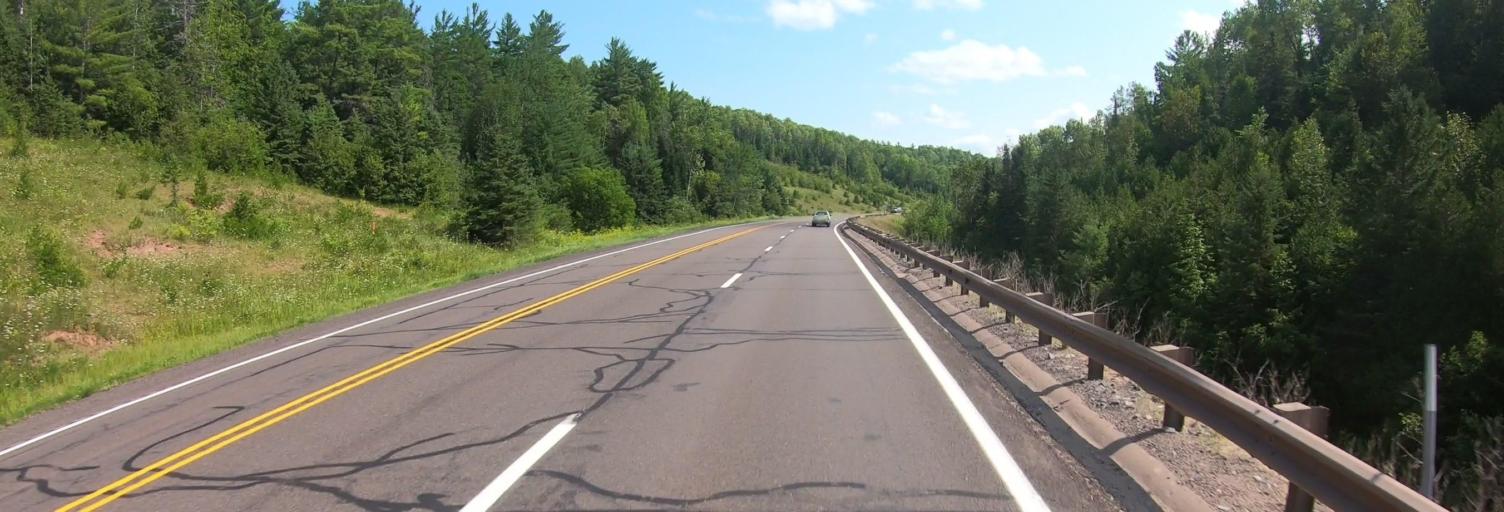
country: US
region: Michigan
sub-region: Ontonagon County
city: Ontonagon
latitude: 46.6894
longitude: -89.1656
